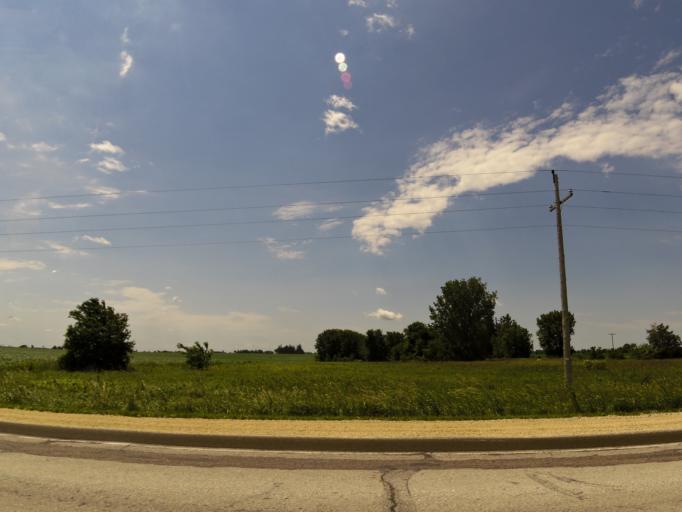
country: US
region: Iowa
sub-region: Bremer County
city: Denver
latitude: 42.7150
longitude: -92.3052
